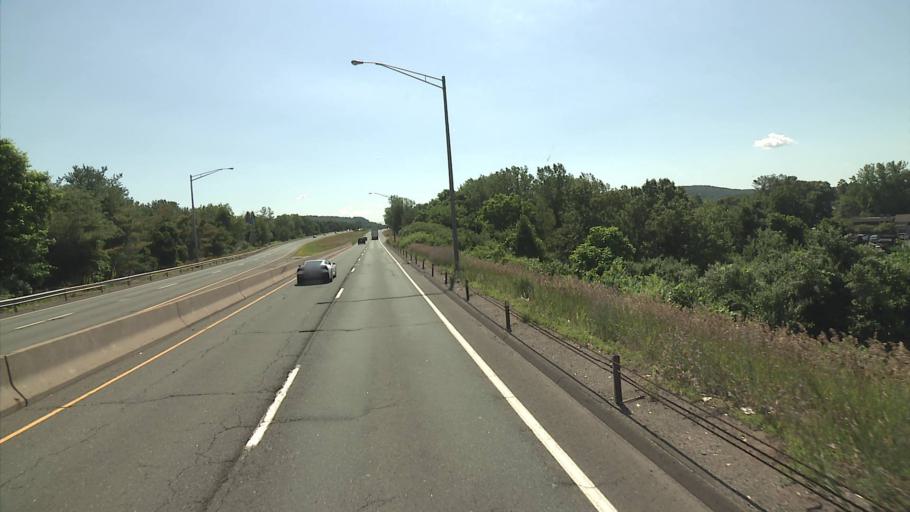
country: US
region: Connecticut
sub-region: Hartford County
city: Plainville
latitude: 41.6771
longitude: -72.8637
